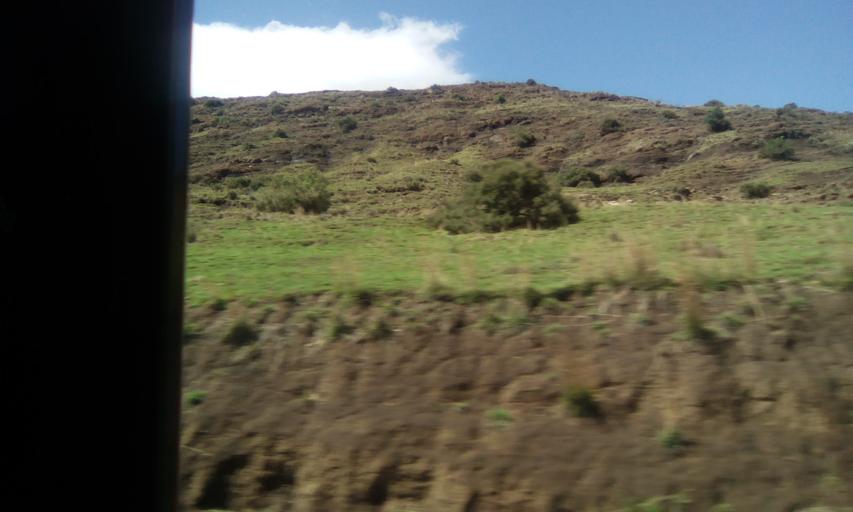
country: LS
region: Maseru
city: Nako
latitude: -29.6567
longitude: 27.8126
